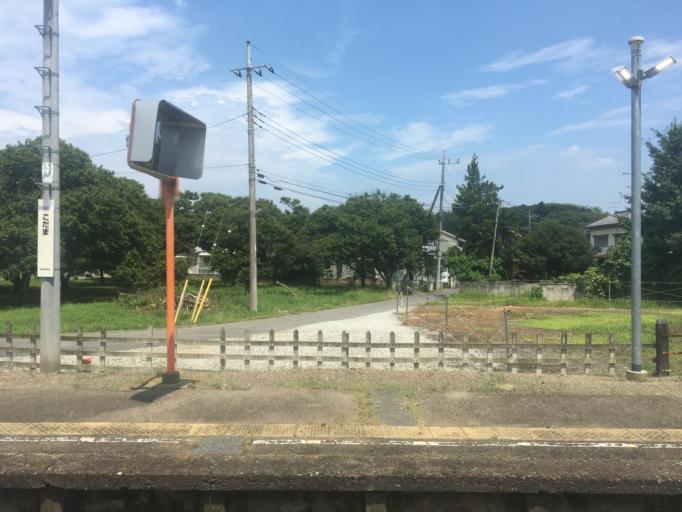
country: JP
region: Saitama
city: Kodamacho-kodamaminami
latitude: 36.1930
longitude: 139.1357
